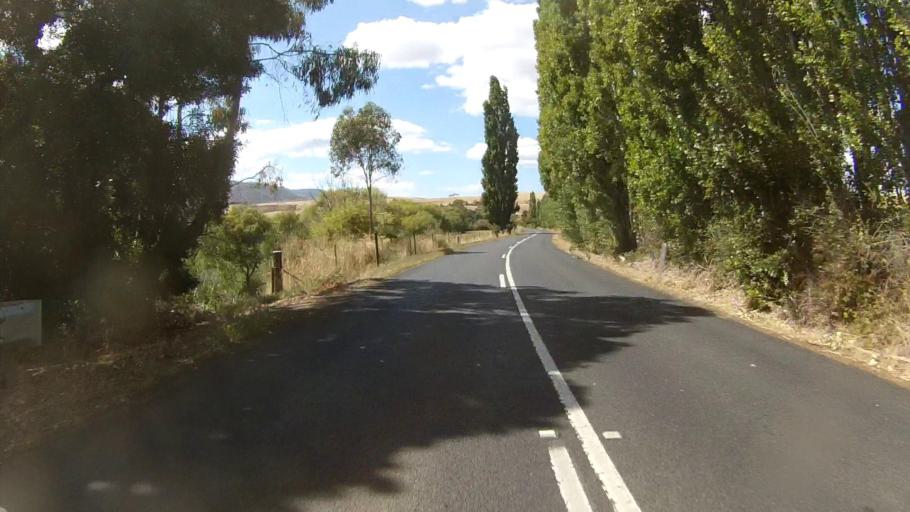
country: AU
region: Tasmania
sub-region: Derwent Valley
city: New Norfolk
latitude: -42.7332
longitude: 146.9170
